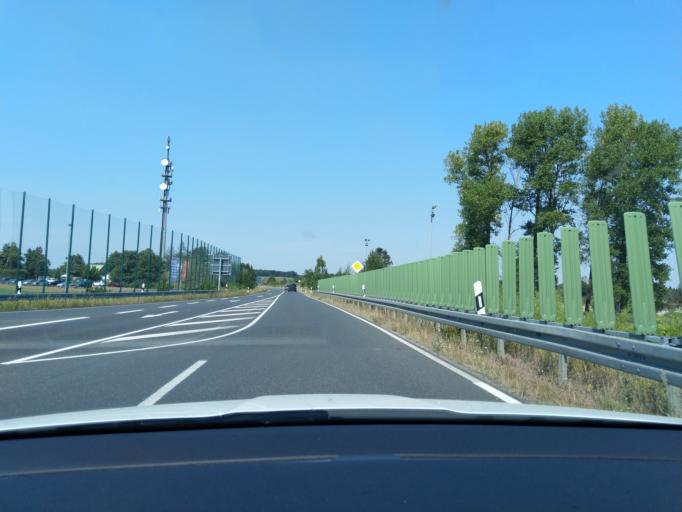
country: DE
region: North Rhine-Westphalia
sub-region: Regierungsbezirk Koln
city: Wassenberg
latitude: 51.1199
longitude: 6.2026
